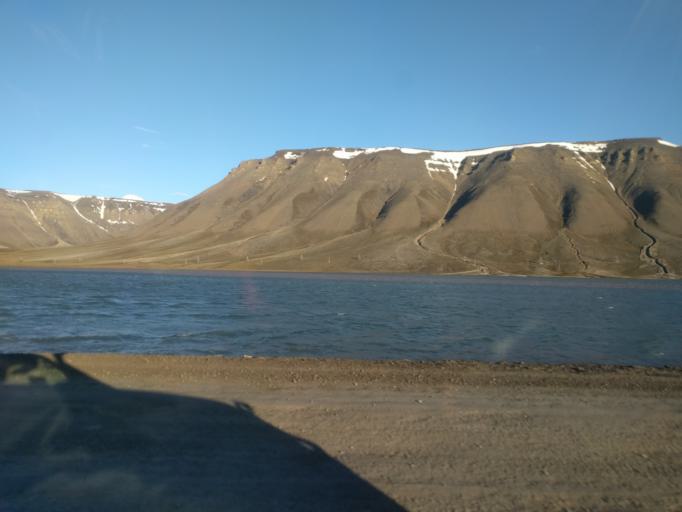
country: SJ
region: Svalbard
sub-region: Spitsbergen
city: Longyearbyen
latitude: 78.2081
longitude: 15.7822
